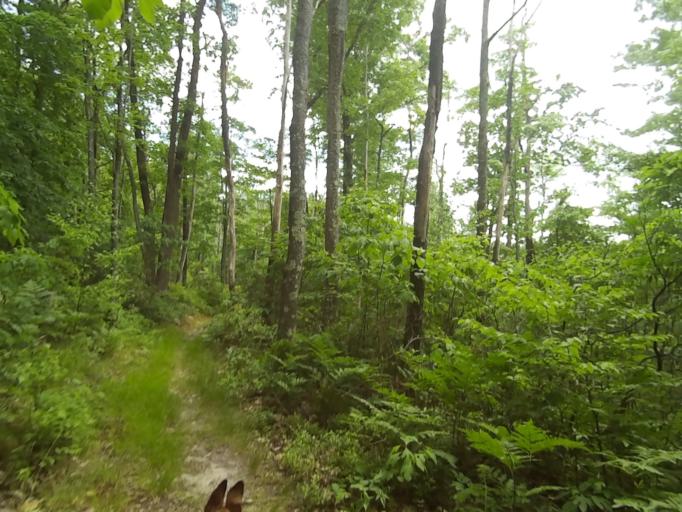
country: US
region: Pennsylvania
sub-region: Centre County
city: Stormstown
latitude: 40.9202
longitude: -78.0569
